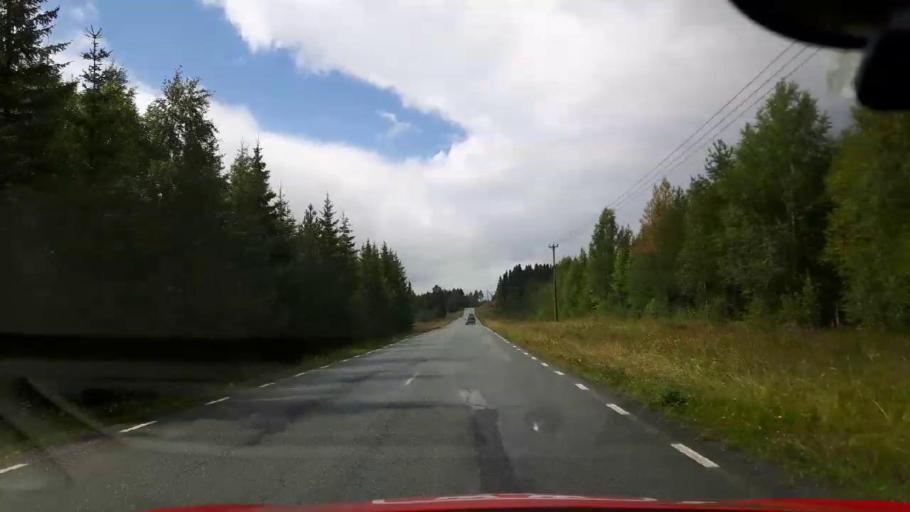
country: SE
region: Jaemtland
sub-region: Krokoms Kommun
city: Krokom
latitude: 63.3506
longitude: 14.2148
